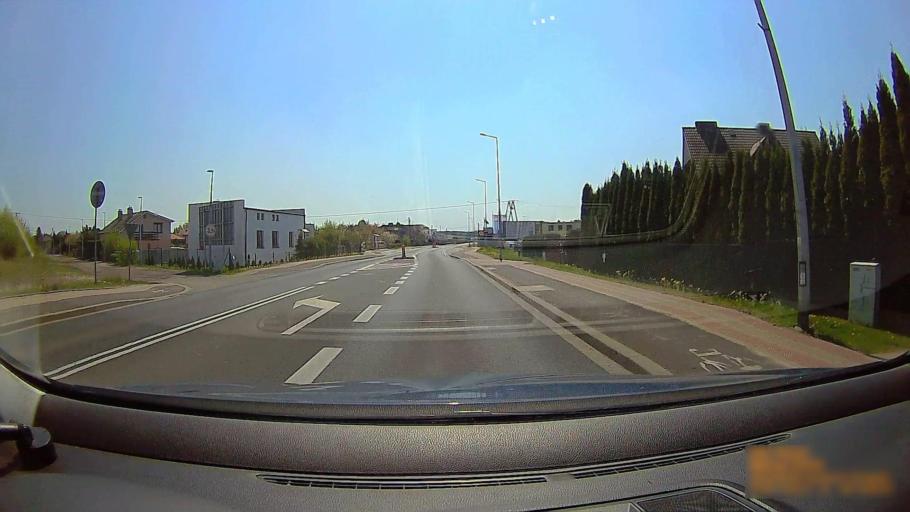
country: PL
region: Greater Poland Voivodeship
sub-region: Konin
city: Konin
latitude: 52.1953
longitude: 18.2622
